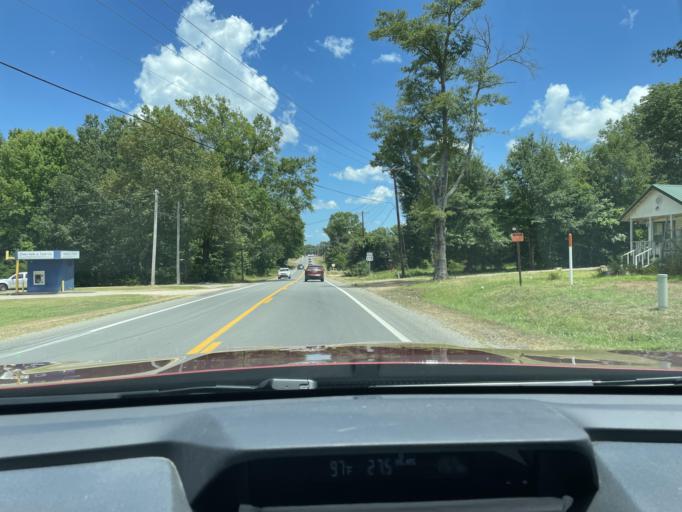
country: US
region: Arkansas
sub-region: Drew County
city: Monticello
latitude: 33.6285
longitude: -91.7743
